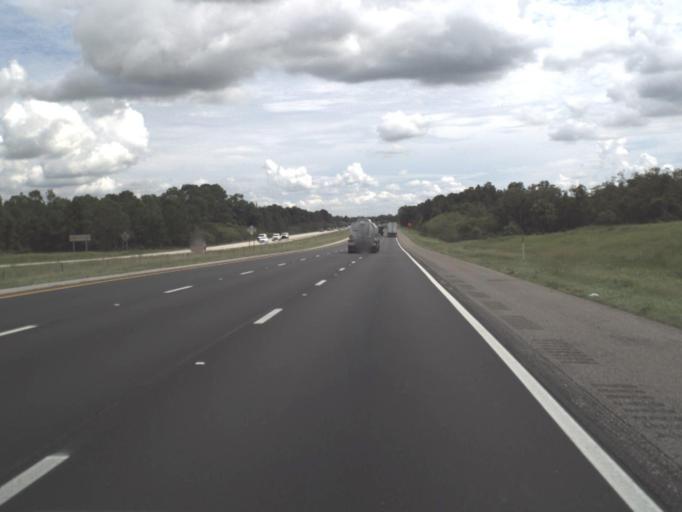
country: US
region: Florida
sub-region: Polk County
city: Davenport
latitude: 28.2034
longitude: -81.6939
